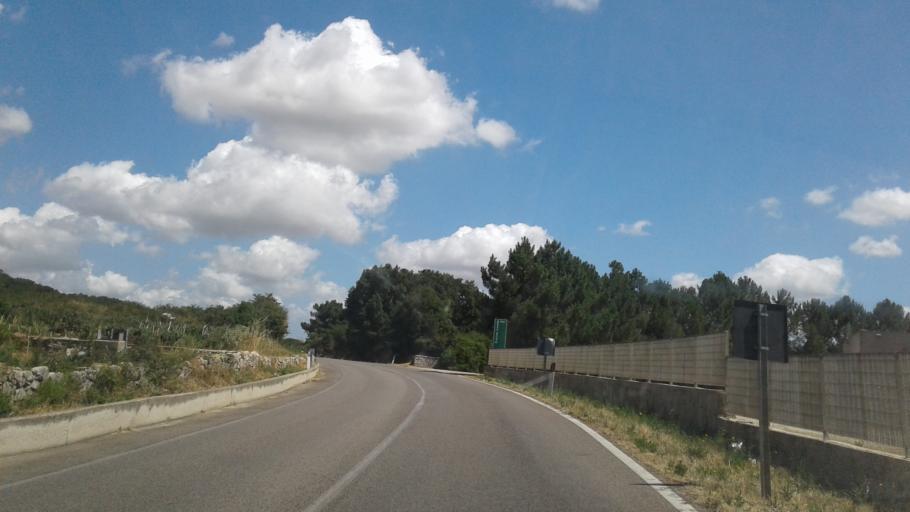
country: IT
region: Sardinia
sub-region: Provincia di Olbia-Tempio
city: Luras
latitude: 40.9064
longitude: 9.1528
